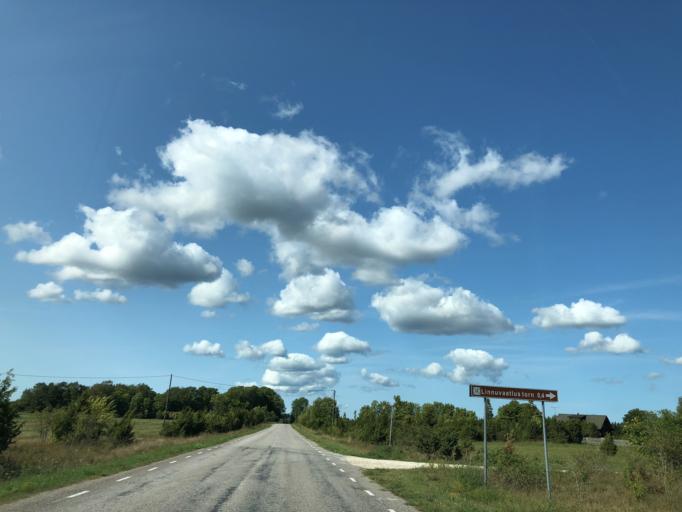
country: EE
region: Hiiumaa
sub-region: Kaerdla linn
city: Kardla
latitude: 58.7935
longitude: 22.7685
